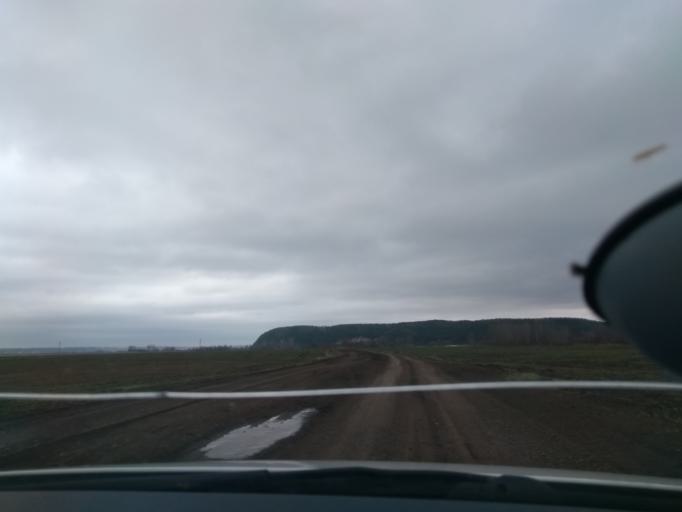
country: RU
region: Perm
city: Orda
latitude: 57.2521
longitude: 56.6232
